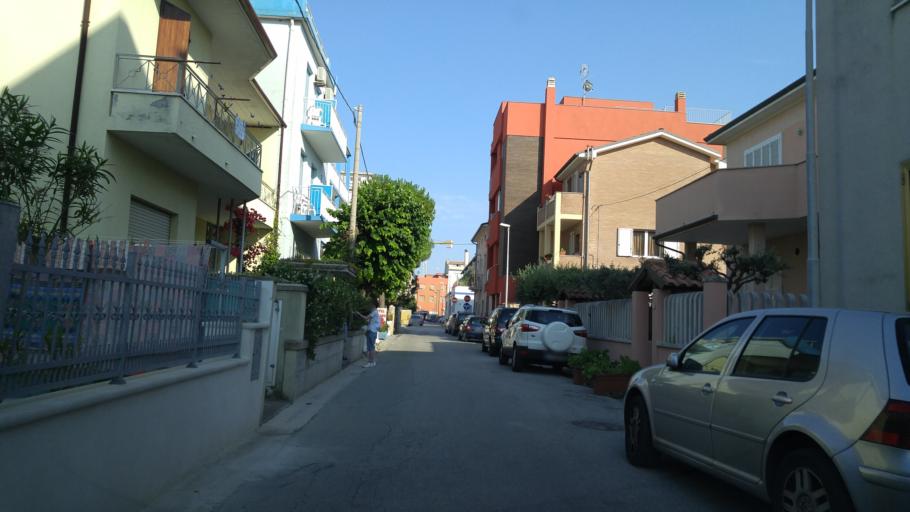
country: IT
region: The Marches
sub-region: Provincia di Pesaro e Urbino
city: Marotta
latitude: 43.7742
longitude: 13.1308
